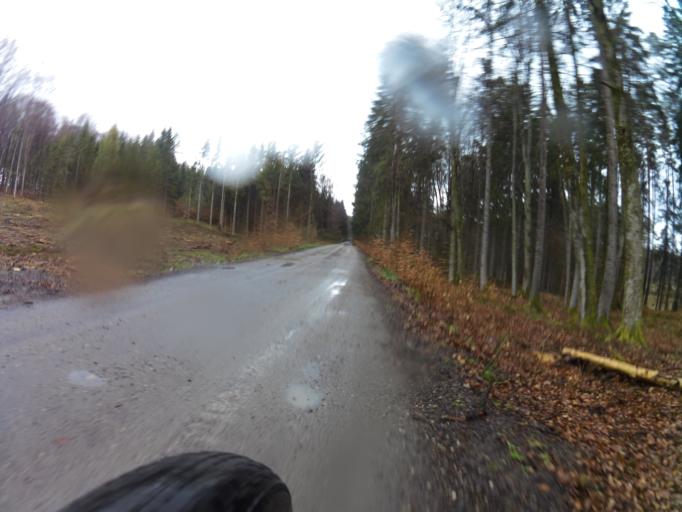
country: PL
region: Pomeranian Voivodeship
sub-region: Powiat slupski
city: Kepice
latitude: 54.2696
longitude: 16.7976
